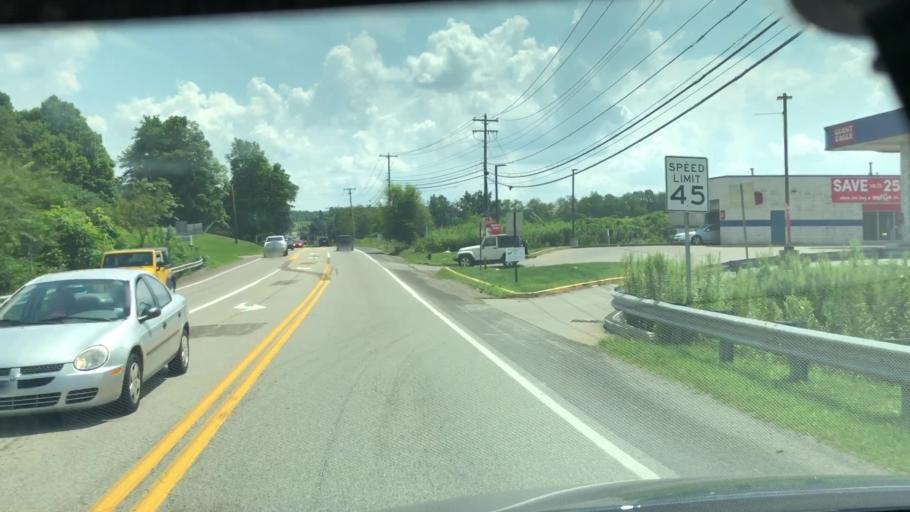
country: US
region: Pennsylvania
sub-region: Armstrong County
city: Freeport
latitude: 40.6992
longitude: -79.7200
